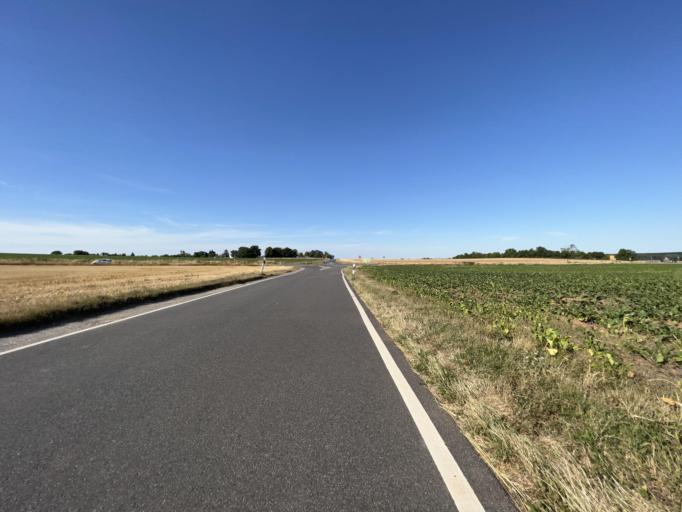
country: DE
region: North Rhine-Westphalia
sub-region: Regierungsbezirk Koln
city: Kreuzau
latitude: 50.7539
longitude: 6.4646
